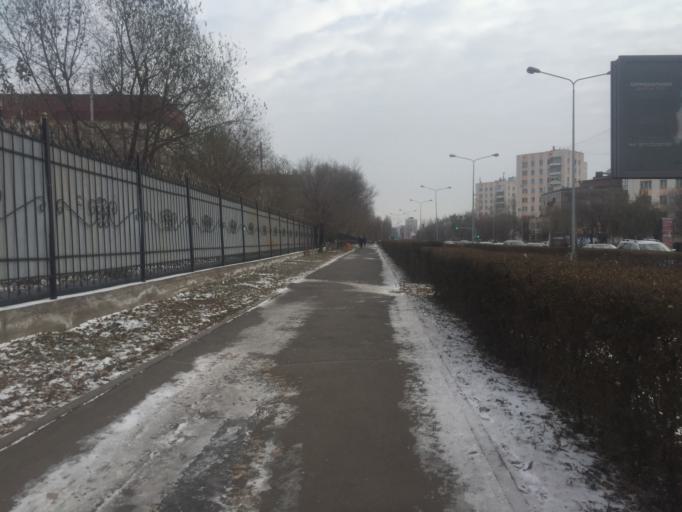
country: KZ
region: Astana Qalasy
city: Astana
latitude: 51.1812
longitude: 71.4100
